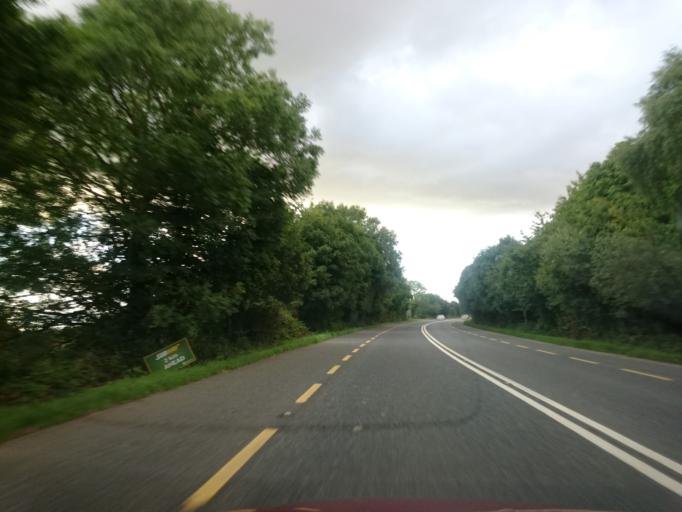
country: IE
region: Leinster
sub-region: Loch Garman
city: Ferns
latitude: 52.5795
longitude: -6.5155
